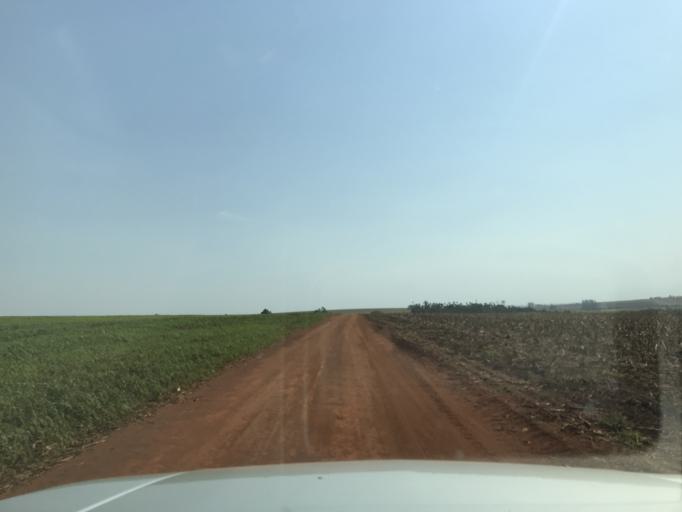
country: BR
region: Parana
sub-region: Palotina
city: Palotina
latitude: -24.2289
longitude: -53.7385
